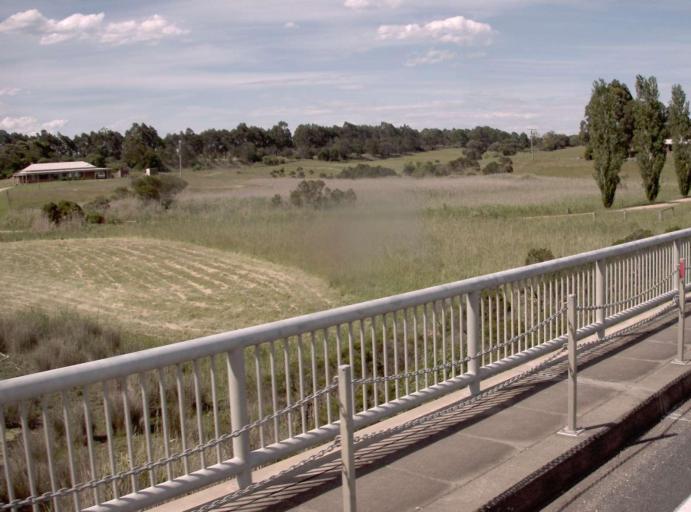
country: AU
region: Victoria
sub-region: East Gippsland
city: Bairnsdale
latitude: -37.8158
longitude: 147.7409
